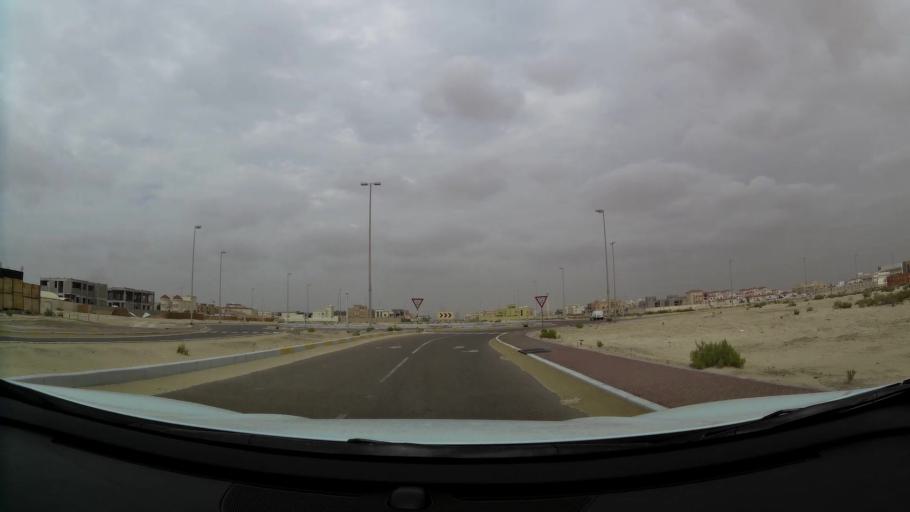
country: AE
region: Abu Dhabi
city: Abu Dhabi
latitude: 24.3916
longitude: 54.6501
